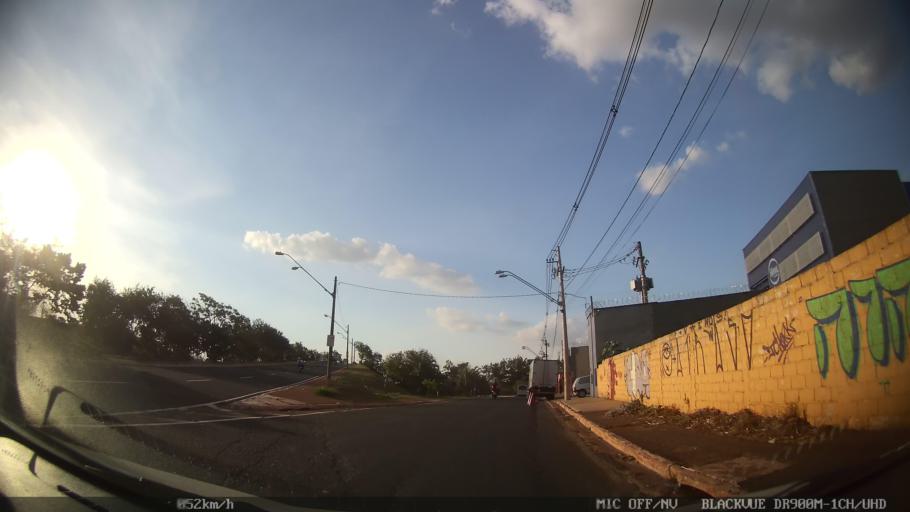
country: BR
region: Sao Paulo
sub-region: Ribeirao Preto
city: Ribeirao Preto
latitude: -21.1391
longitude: -47.8030
